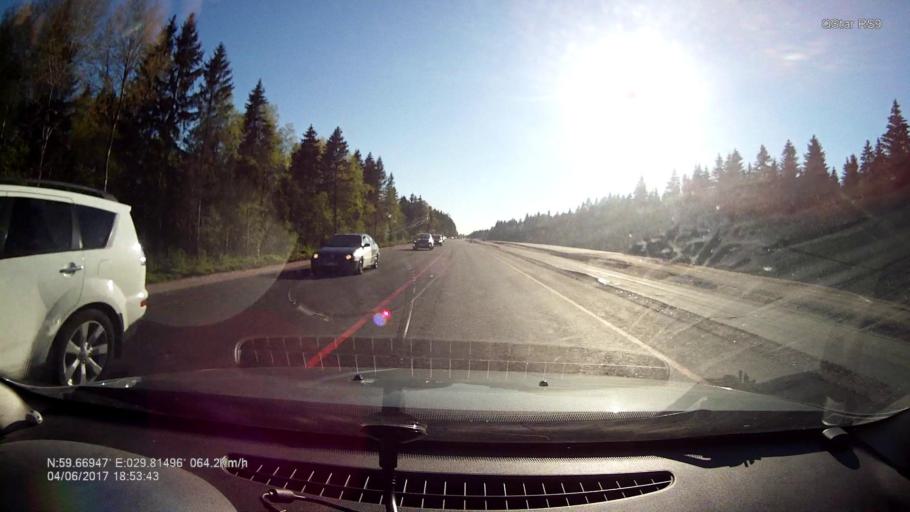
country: RU
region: Leningrad
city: Kipen'
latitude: 59.6694
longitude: 29.8147
